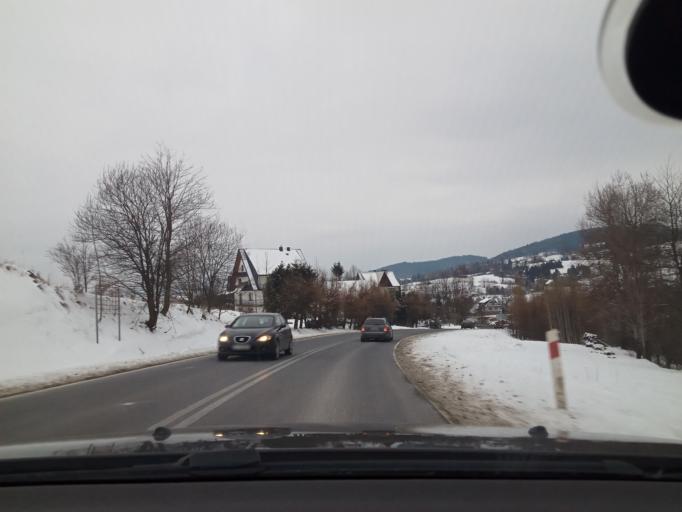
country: PL
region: Lesser Poland Voivodeship
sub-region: Powiat limanowski
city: Lubomierz
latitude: 49.6050
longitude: 20.2094
